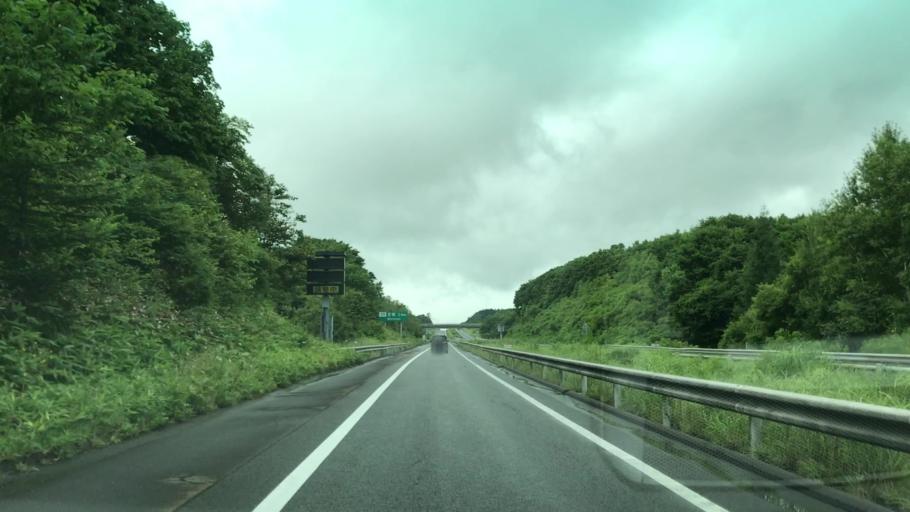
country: JP
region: Hokkaido
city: Muroran
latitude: 42.3836
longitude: 140.9986
